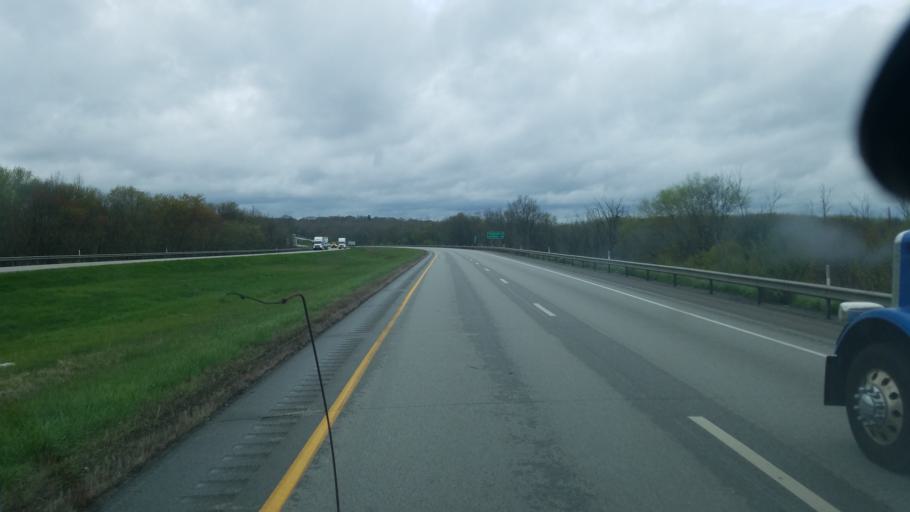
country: US
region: Pennsylvania
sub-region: Mercer County
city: Farrell
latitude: 41.1838
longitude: -80.4618
